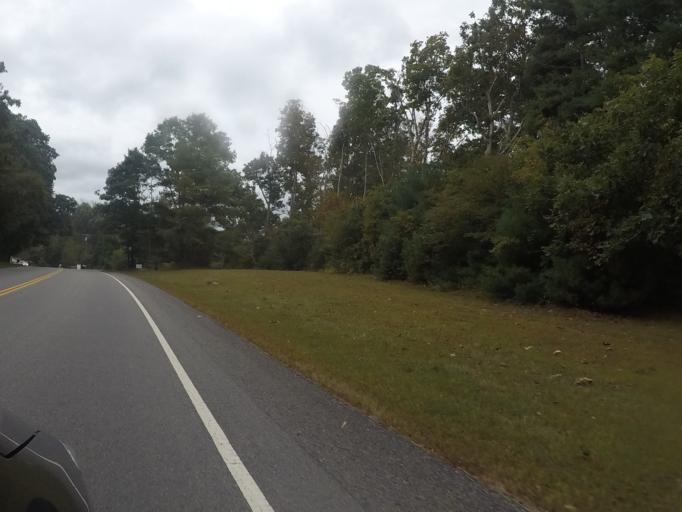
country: US
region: Massachusetts
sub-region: Bristol County
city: Smith Mills
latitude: 41.5975
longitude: -71.0025
